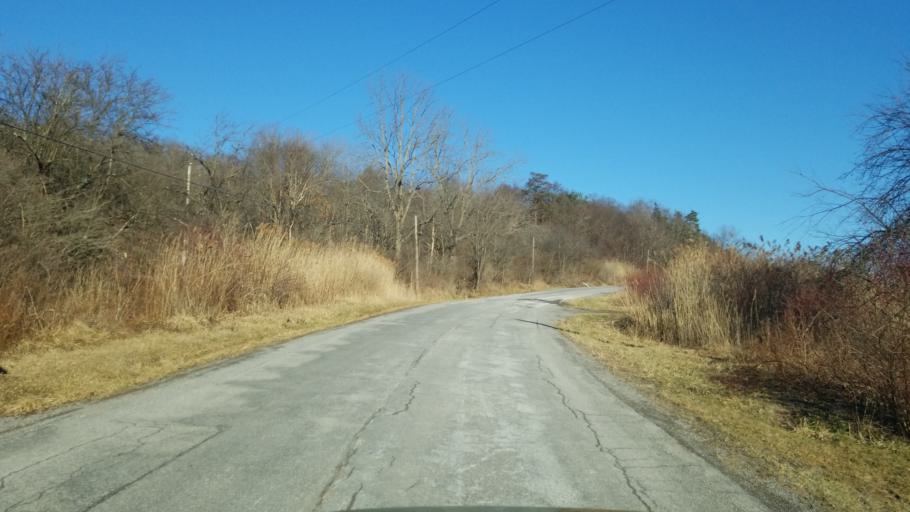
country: US
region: Pennsylvania
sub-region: Jefferson County
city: Sykesville
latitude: 41.0473
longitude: -78.7721
